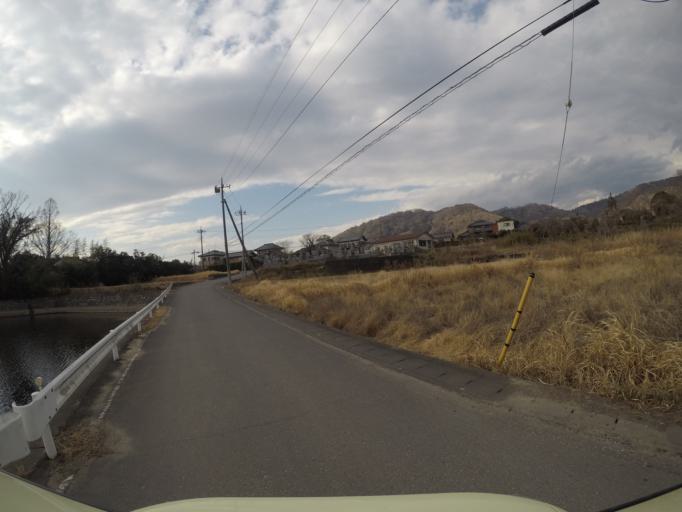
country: JP
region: Ibaraki
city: Tsukuba
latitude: 36.1764
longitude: 140.1131
